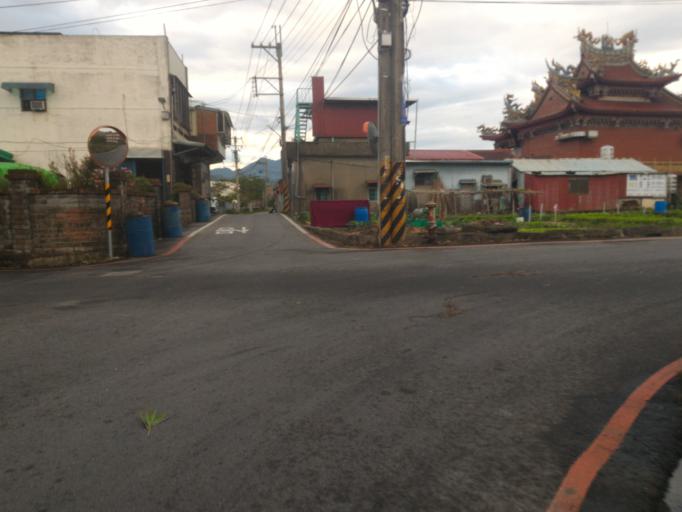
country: TW
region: Taiwan
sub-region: Taoyuan
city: Taoyuan
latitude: 24.9423
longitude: 121.3854
